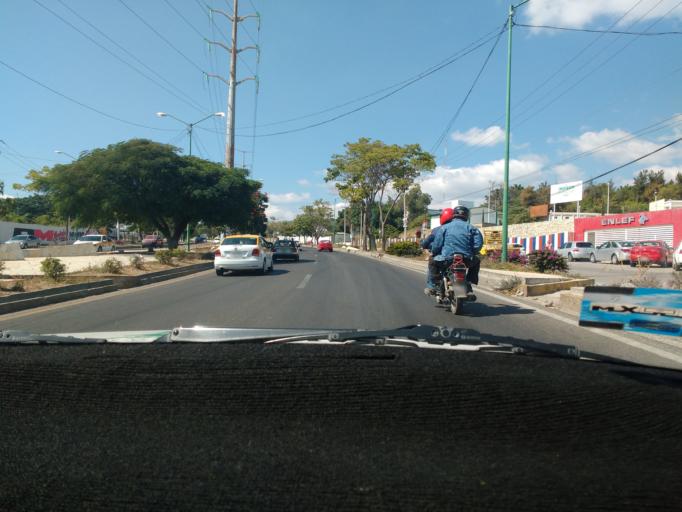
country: MX
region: Chiapas
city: Tuxtla Gutierrez
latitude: 16.7745
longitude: -93.1240
